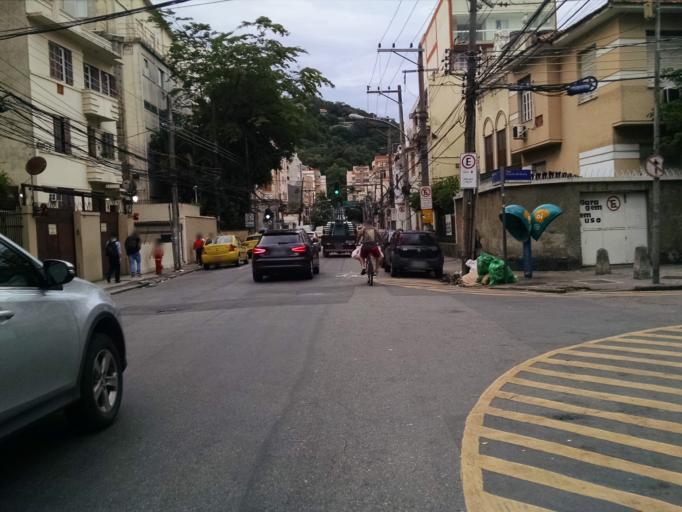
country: BR
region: Rio de Janeiro
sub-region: Rio De Janeiro
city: Rio de Janeiro
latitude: -22.9470
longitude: -43.1858
